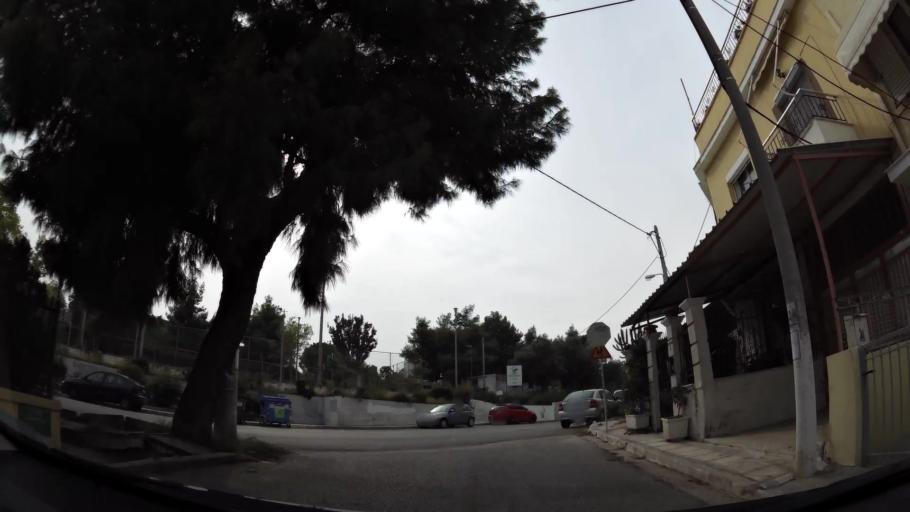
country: GR
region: Attica
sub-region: Nomarchia Athinas
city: Nea Ionia
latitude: 38.0312
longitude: 23.7547
